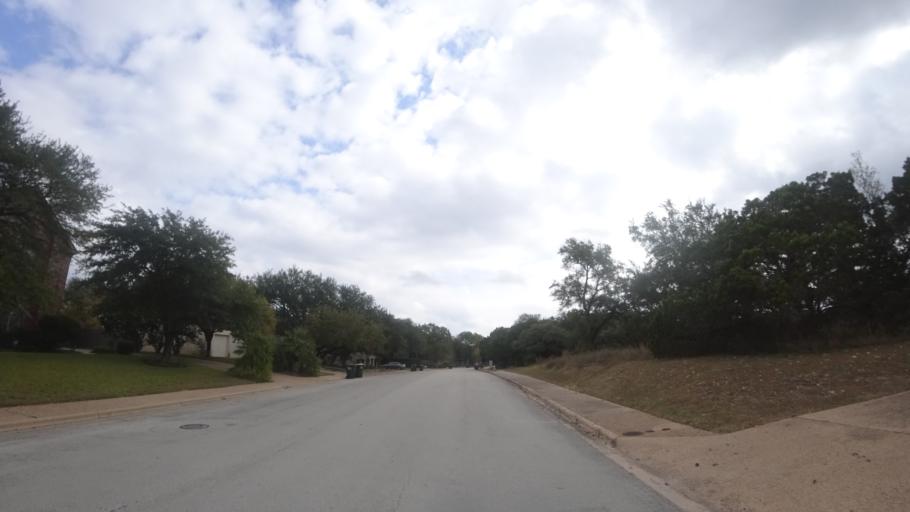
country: US
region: Texas
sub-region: Travis County
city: Barton Creek
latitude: 30.2956
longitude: -97.8866
